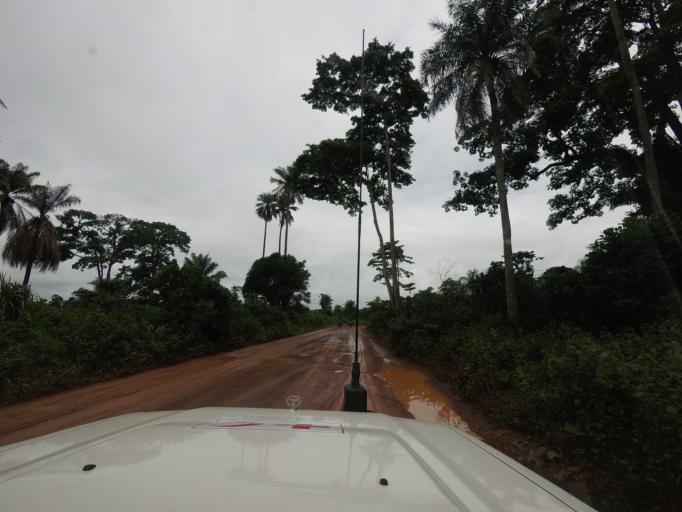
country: GN
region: Nzerekore
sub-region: Nzerekore Prefecture
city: Nzerekore
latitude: 7.7291
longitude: -8.8497
